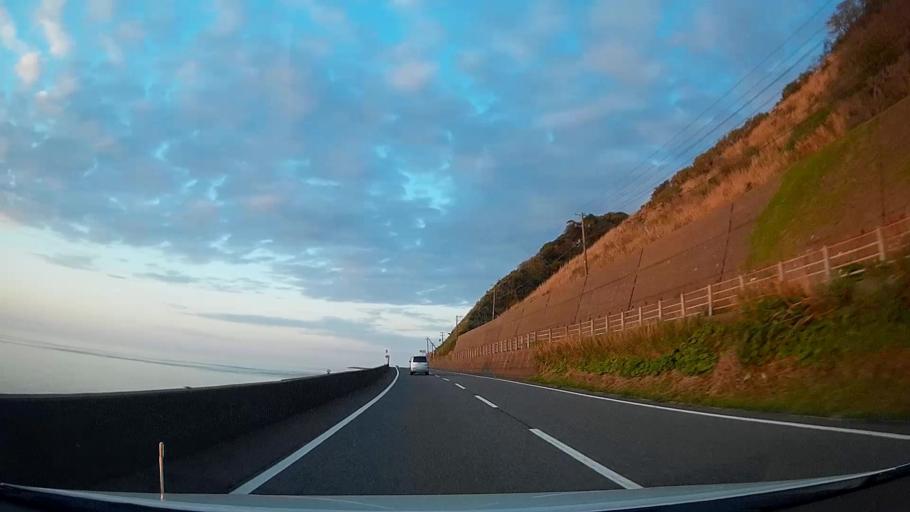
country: JP
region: Niigata
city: Joetsu
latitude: 37.1469
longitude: 138.0667
